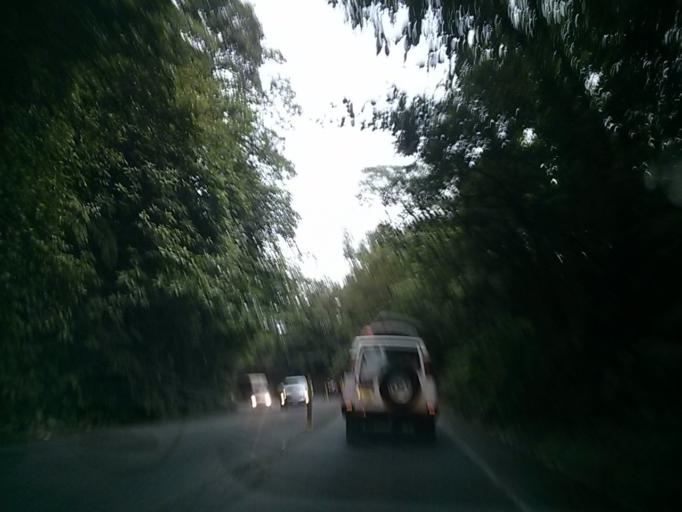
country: CR
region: San Jose
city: Dulce Nombre de Jesus
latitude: 10.1403
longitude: -83.9731
